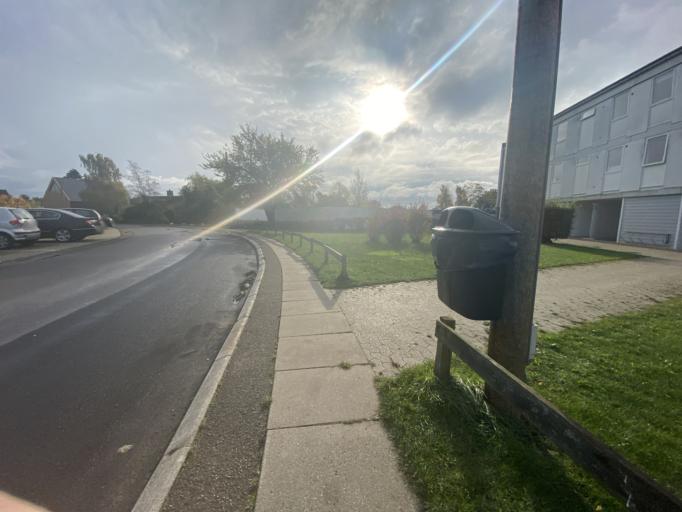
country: DK
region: Capital Region
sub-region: Dragor Kommune
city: Dragor
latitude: 55.5828
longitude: 12.6475
